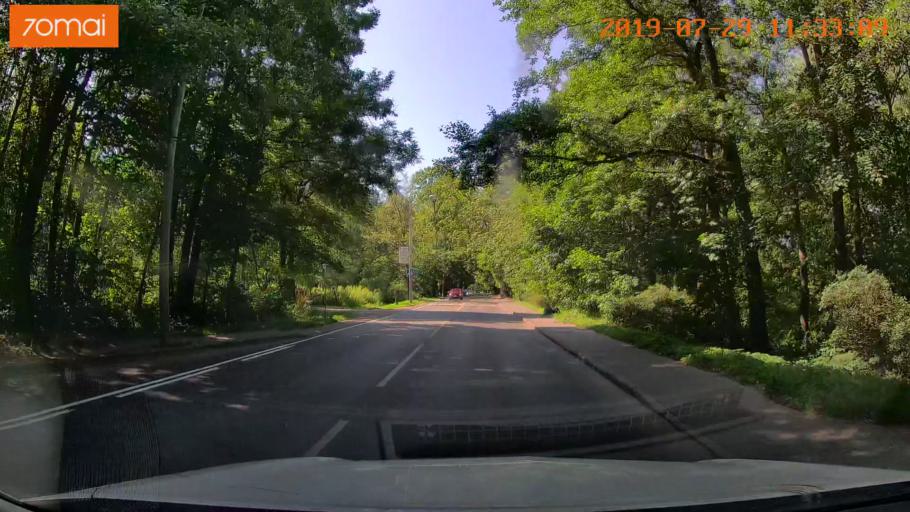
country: RU
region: Kaliningrad
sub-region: Gorod Kaliningrad
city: Kaliningrad
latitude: 54.6666
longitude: 20.5427
